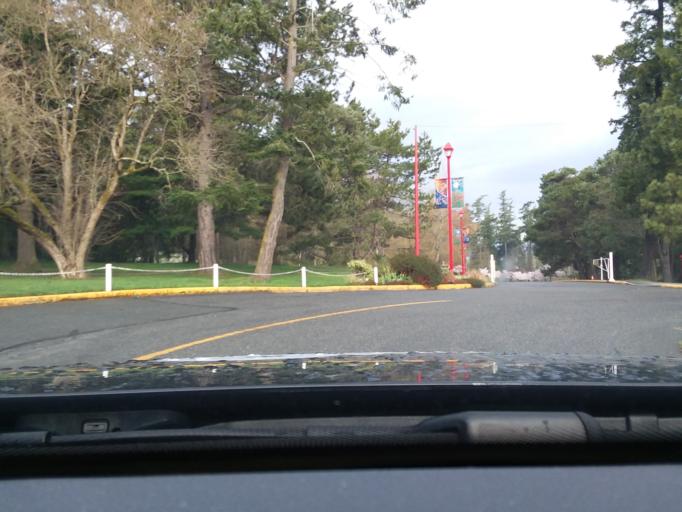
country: CA
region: British Columbia
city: Victoria
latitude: 48.4455
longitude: -123.4011
